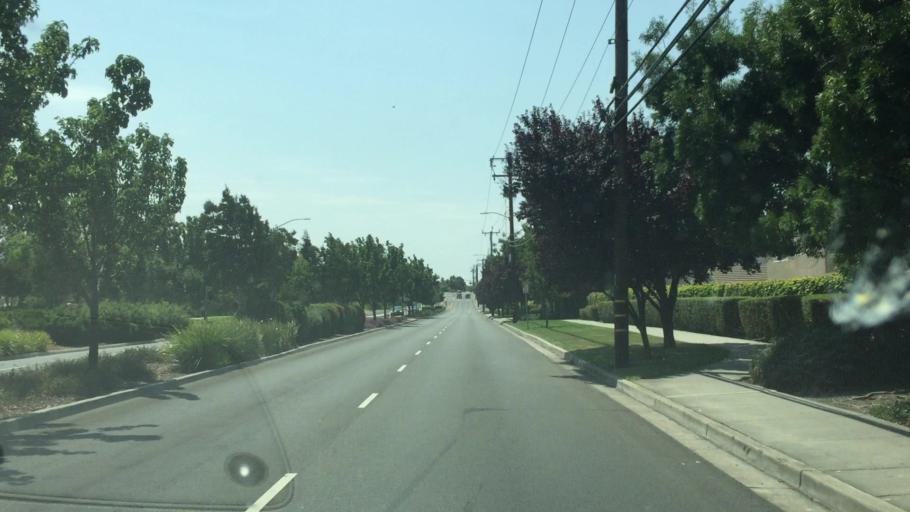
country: US
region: California
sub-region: Napa County
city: American Canyon
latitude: 38.1612
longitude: -122.2397
